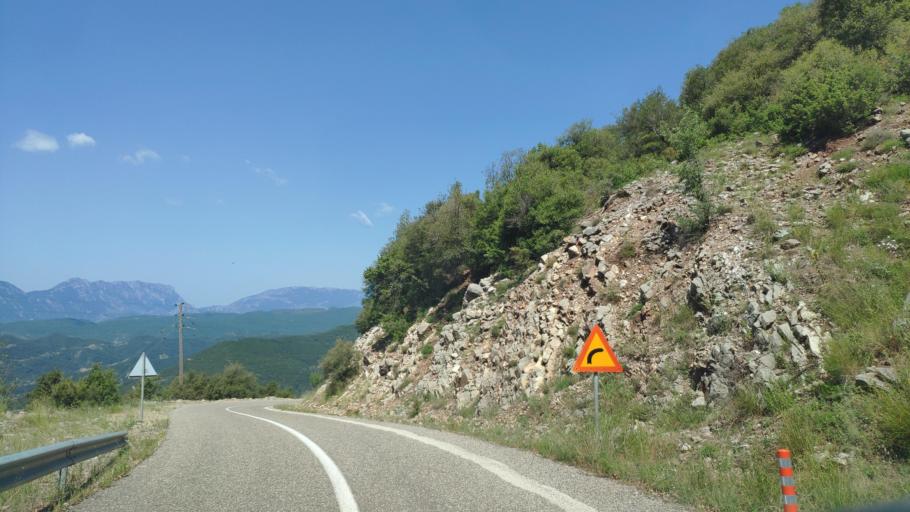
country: GR
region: Central Greece
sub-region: Nomos Evrytanias
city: Kerasochori
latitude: 39.0067
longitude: 21.5954
